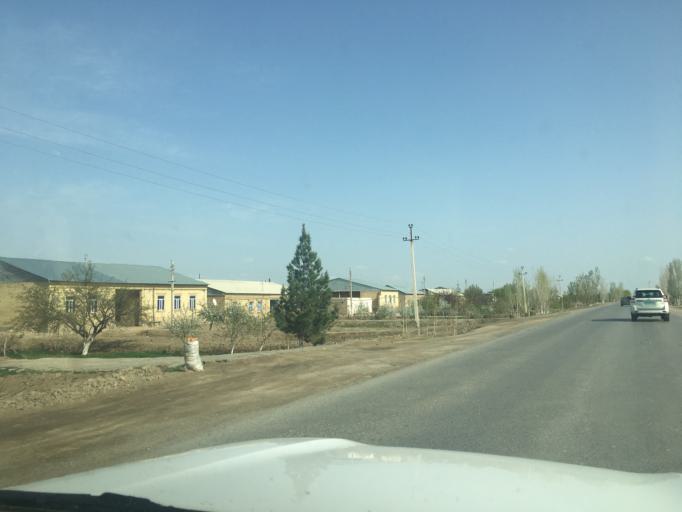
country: TM
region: Lebap
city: Farap
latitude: 39.2022
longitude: 63.5625
